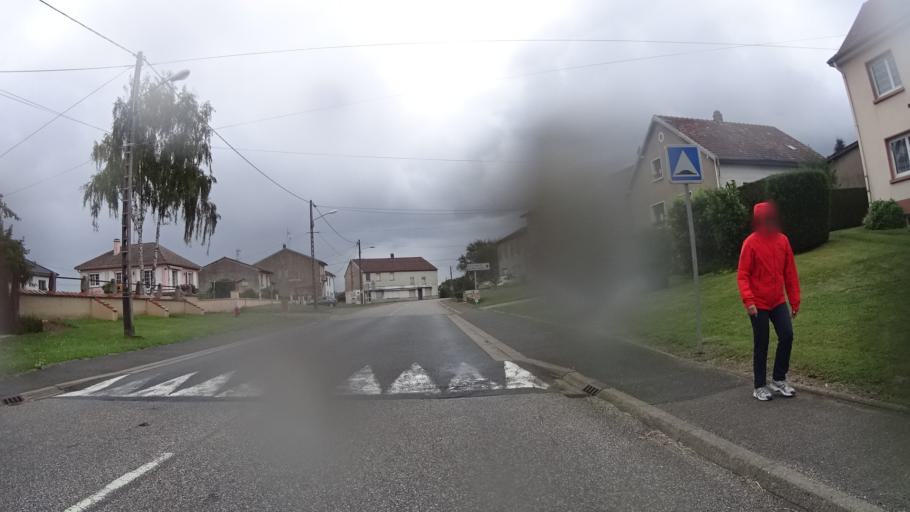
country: FR
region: Lorraine
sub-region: Departement de la Moselle
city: Dieuze
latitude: 48.6734
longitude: 6.7834
